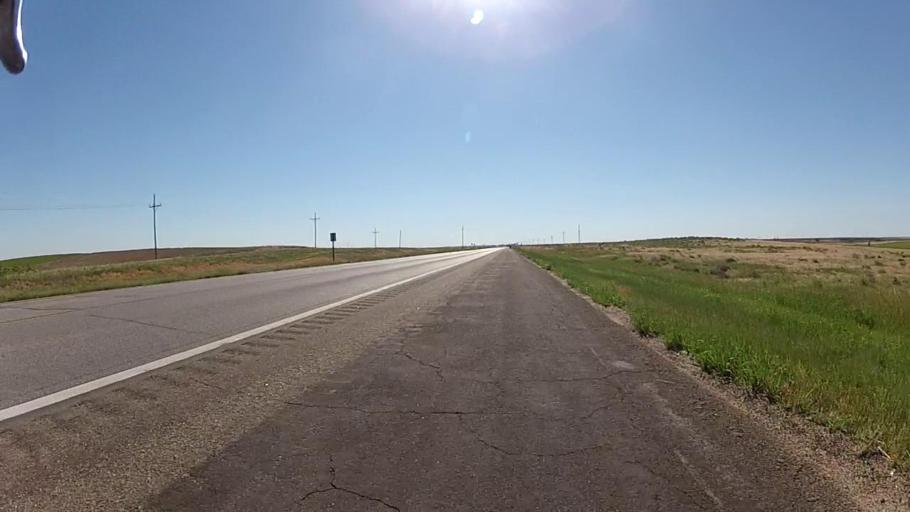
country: US
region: Kansas
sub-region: Kiowa County
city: Greensburg
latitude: 37.5864
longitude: -99.5605
